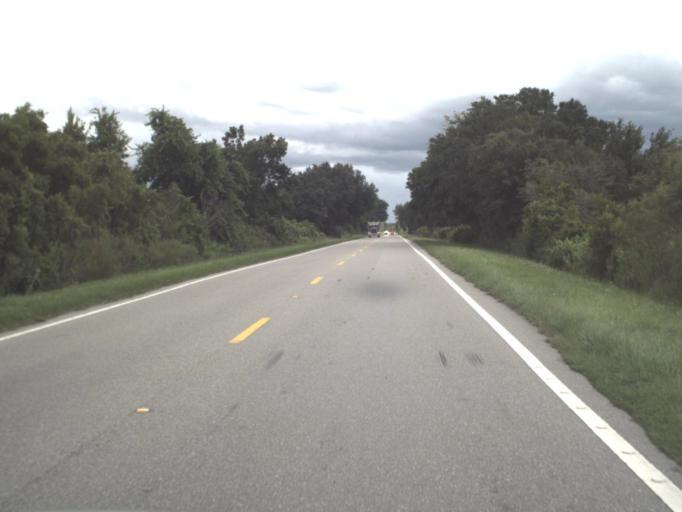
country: US
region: Florida
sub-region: Hillsborough County
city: Balm
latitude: 27.6377
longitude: -82.0645
